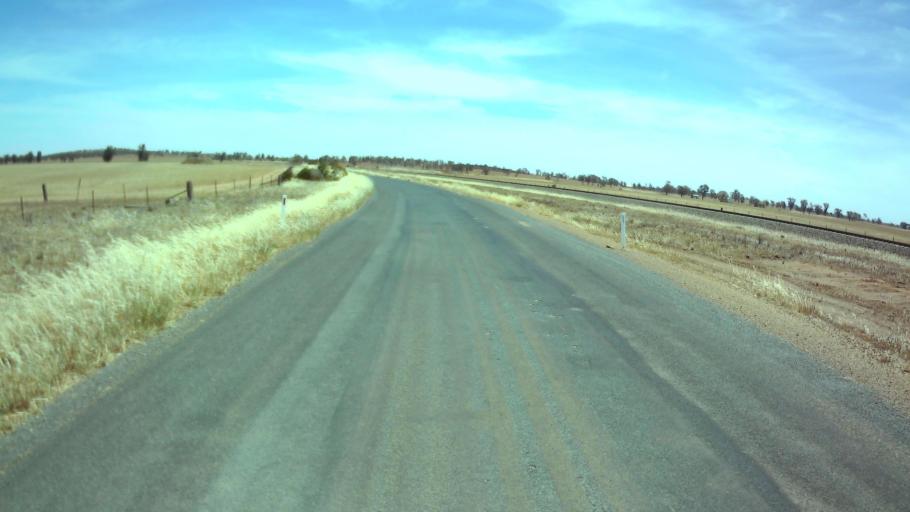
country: AU
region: New South Wales
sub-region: Weddin
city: Grenfell
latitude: -33.7551
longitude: 147.7635
